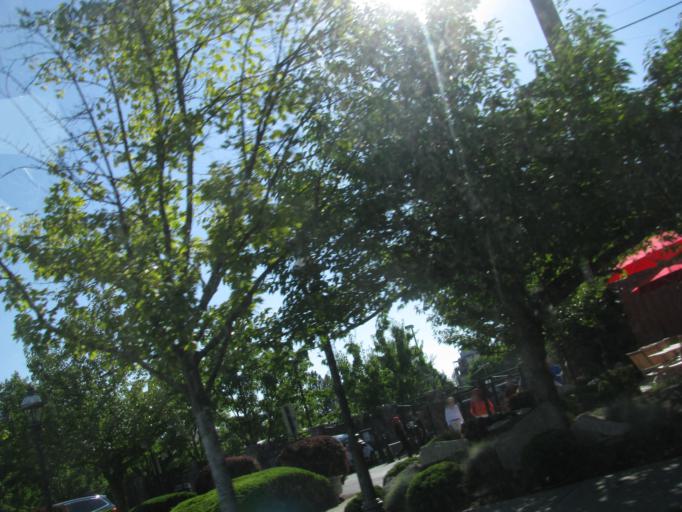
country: US
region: Washington
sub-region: Spokane County
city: Spokane
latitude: 47.6656
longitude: -117.4176
